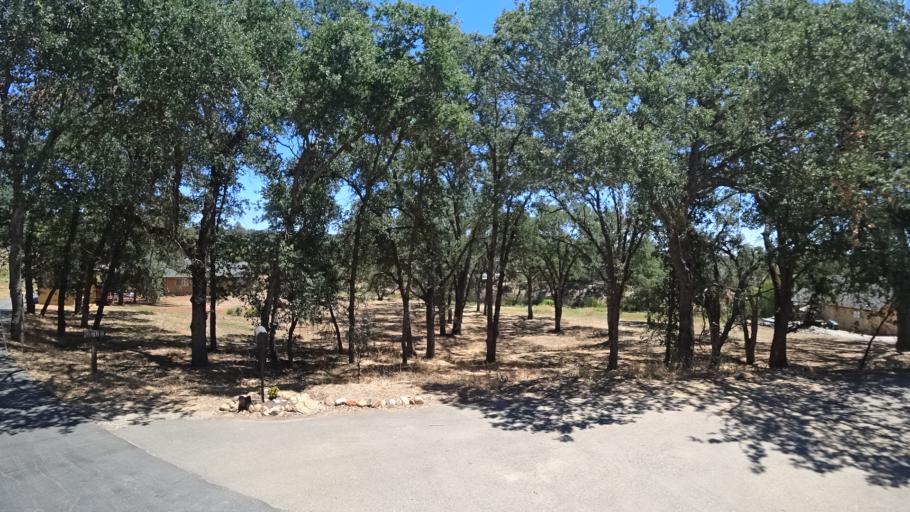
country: US
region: California
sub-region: Calaveras County
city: Valley Springs
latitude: 38.1612
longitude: -120.8371
